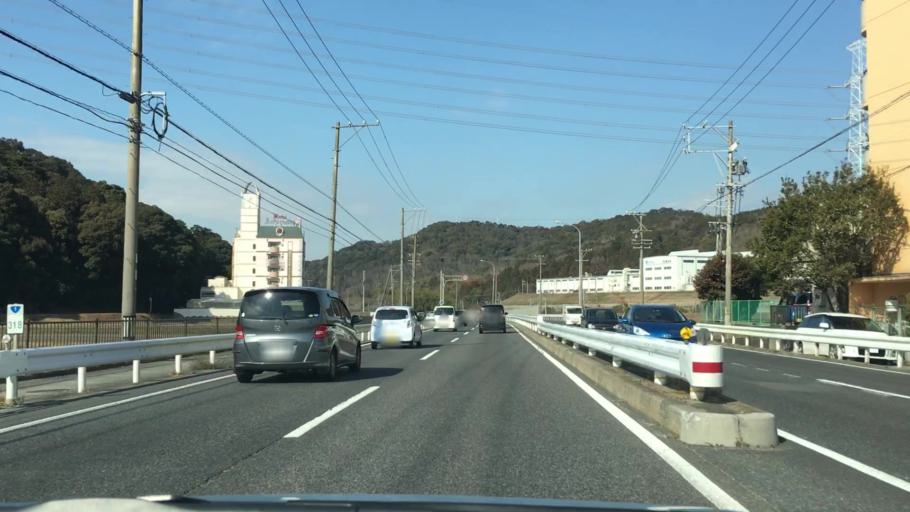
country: JP
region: Aichi
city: Gamagori
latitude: 34.9038
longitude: 137.2350
